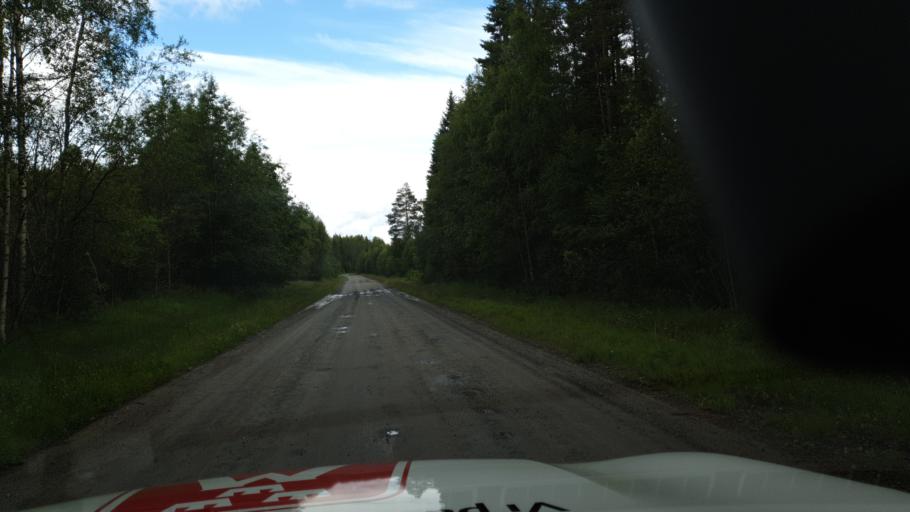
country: SE
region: Vaesterbotten
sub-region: Robertsfors Kommun
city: Robertsfors
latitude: 64.2207
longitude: 21.0703
